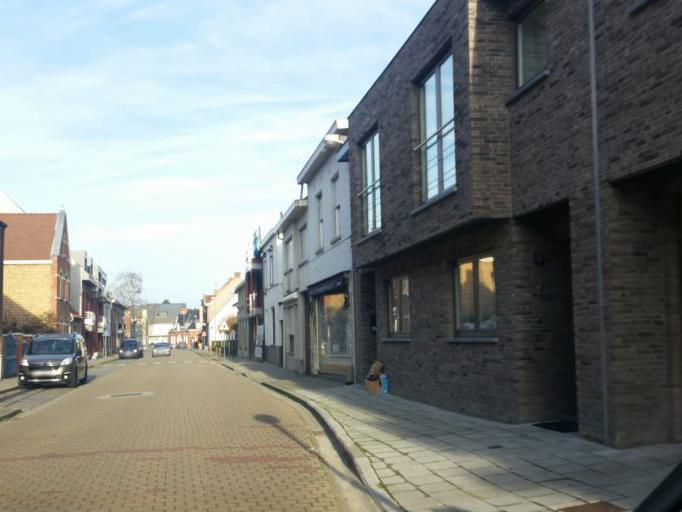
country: BE
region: Flanders
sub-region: Provincie West-Vlaanderen
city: Damme
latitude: 51.2036
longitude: 3.3204
